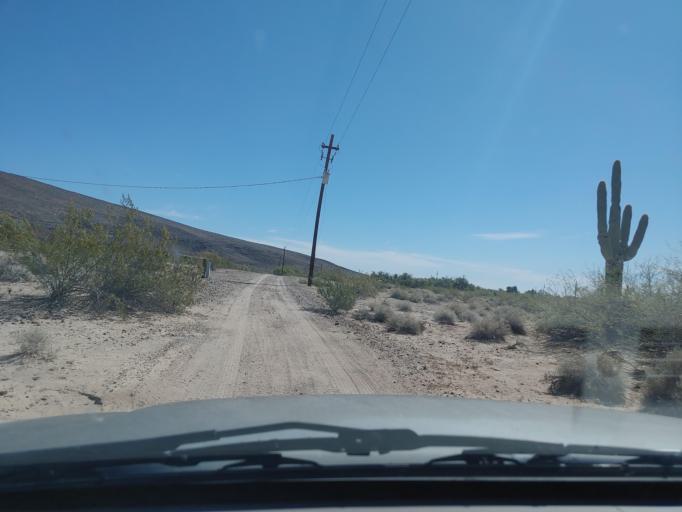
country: US
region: Arizona
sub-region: Maricopa County
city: Gila Bend
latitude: 32.9887
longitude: -113.3394
